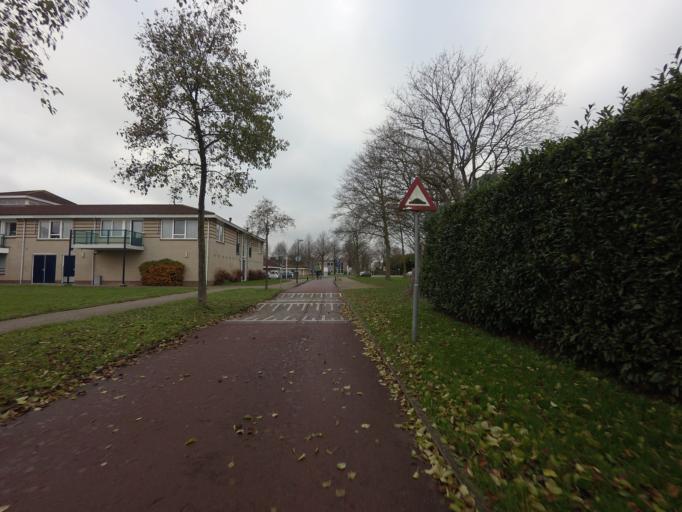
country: NL
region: Utrecht
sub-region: Gemeente Houten
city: Houten
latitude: 52.0237
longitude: 5.1657
